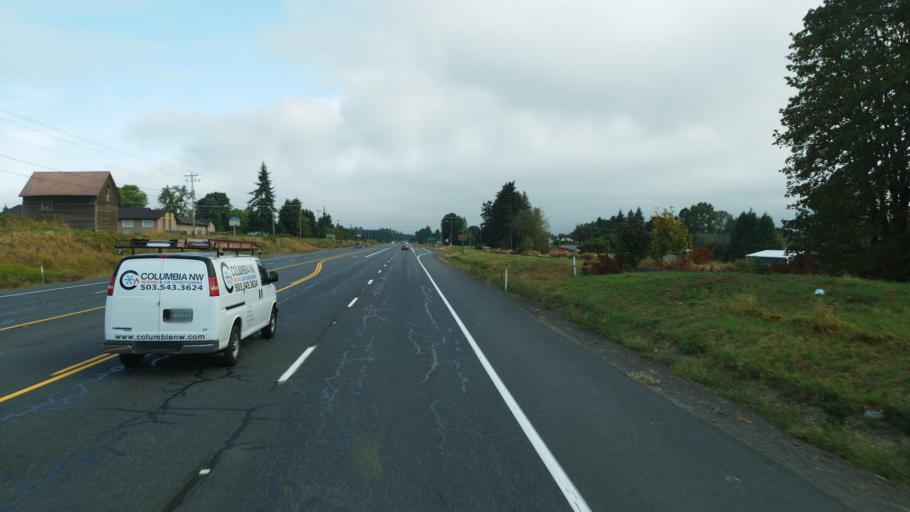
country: US
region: Oregon
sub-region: Columbia County
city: Scappoose
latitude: 45.7779
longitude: -122.8763
